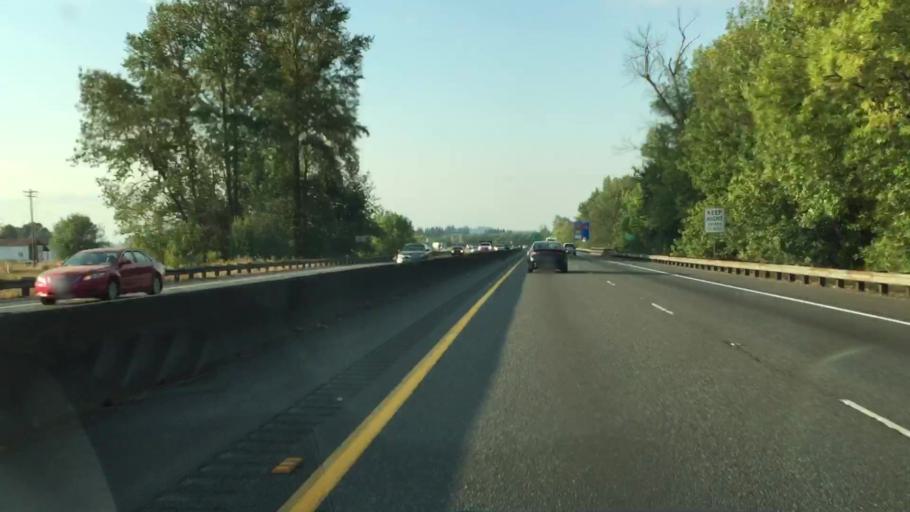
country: US
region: Washington
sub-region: Lewis County
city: Chehalis
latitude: 46.6901
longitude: -122.9701
